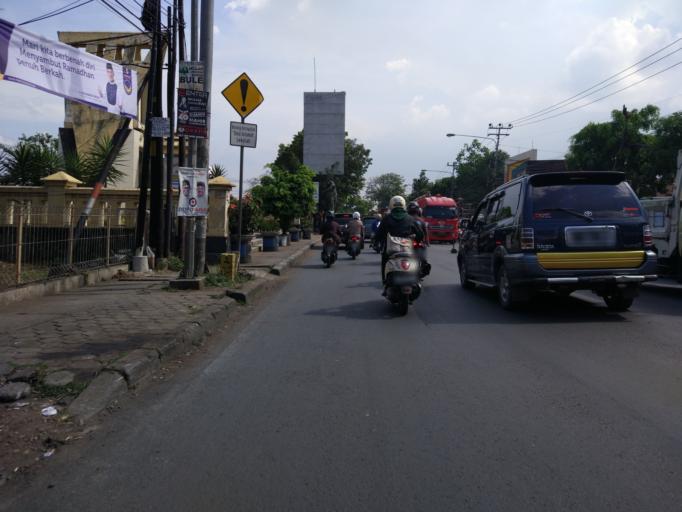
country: ID
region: West Java
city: Cileunyi
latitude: -6.9339
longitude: 107.7223
